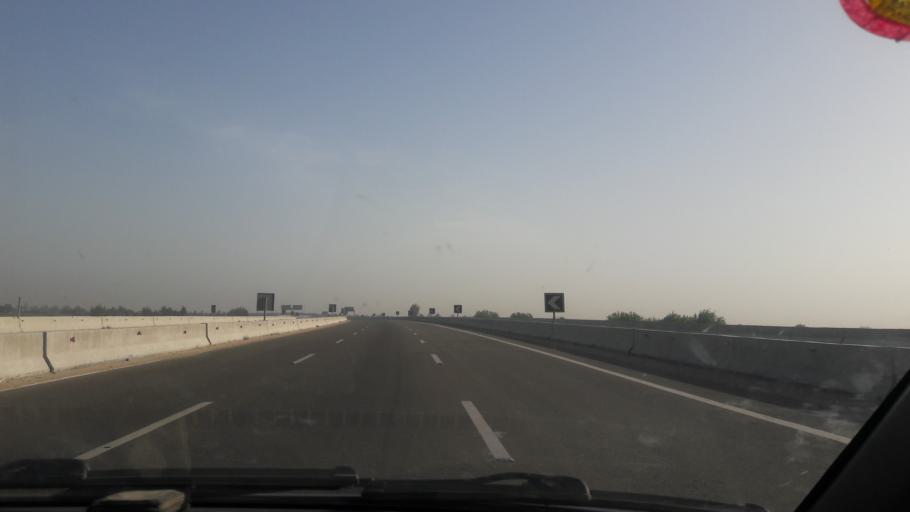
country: EG
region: Al Isma'iliyah
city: Ismailia
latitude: 30.7936
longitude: 32.1646
